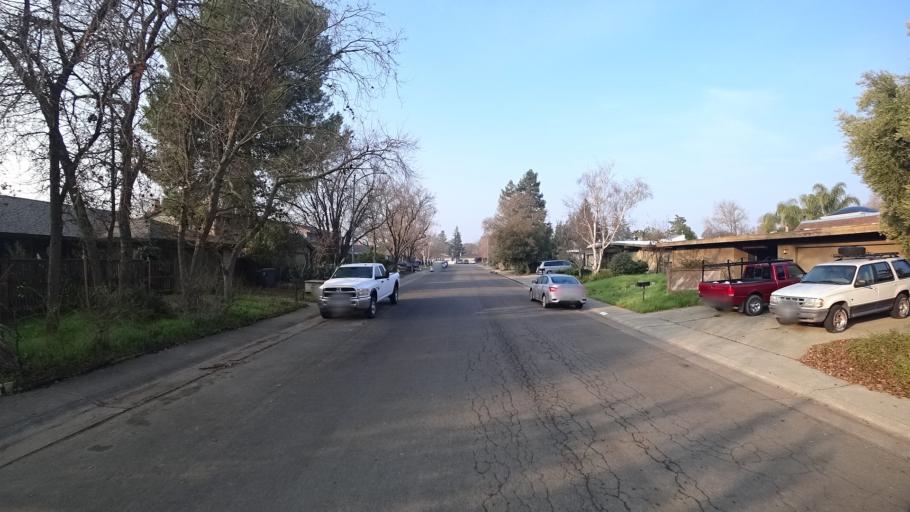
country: US
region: California
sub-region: Yolo County
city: Davis
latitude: 38.5669
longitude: -121.7526
